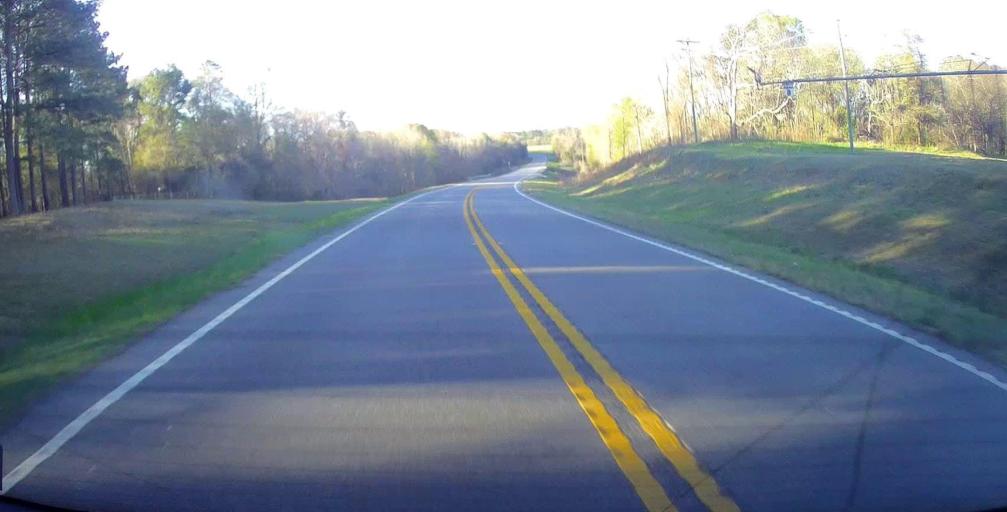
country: US
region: Georgia
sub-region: Pulaski County
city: Hawkinsville
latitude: 32.2479
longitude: -83.4104
